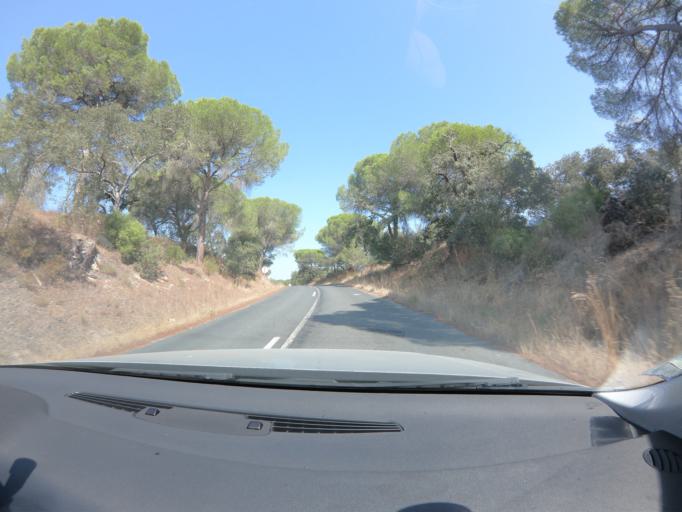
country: PT
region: Setubal
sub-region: Alcacer do Sal
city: Alcacer do Sal
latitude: 38.2975
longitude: -8.4044
